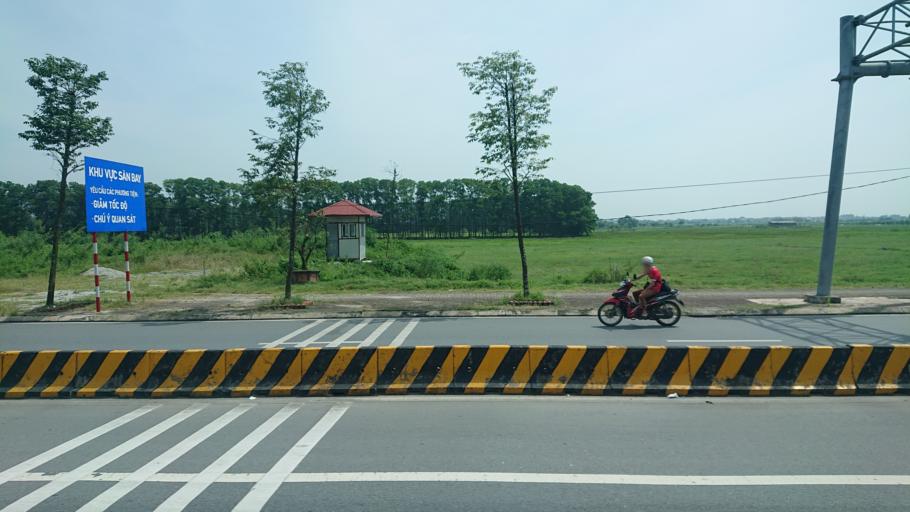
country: VN
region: Ha Noi
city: Soc Son
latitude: 21.2071
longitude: 105.8238
